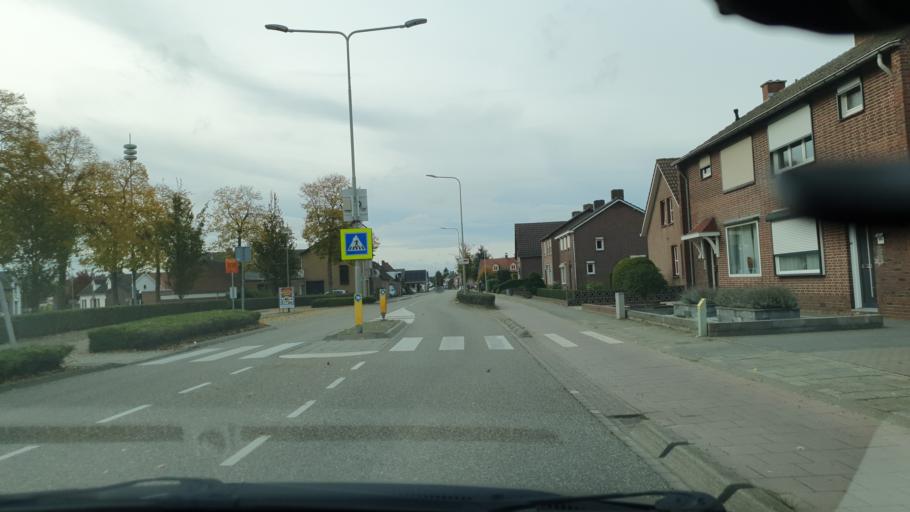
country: NL
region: Limburg
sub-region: Gemeente Maasgouw
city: Maasbracht
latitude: 51.0937
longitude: 5.8994
